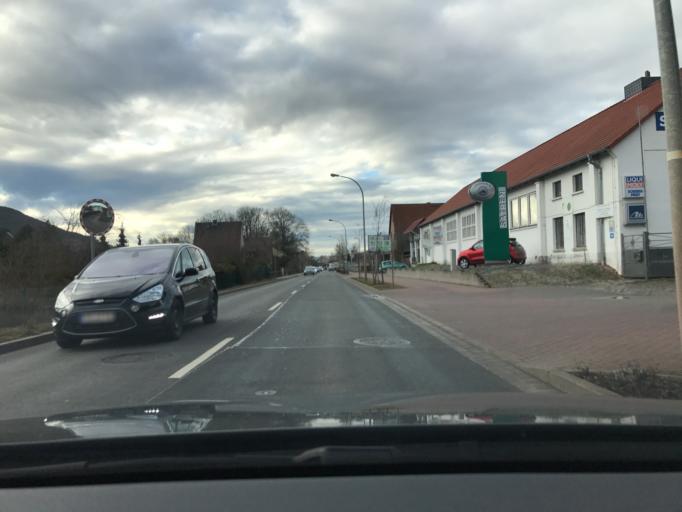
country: DE
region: Thuringia
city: Sondershausen
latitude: 51.3774
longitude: 10.8653
